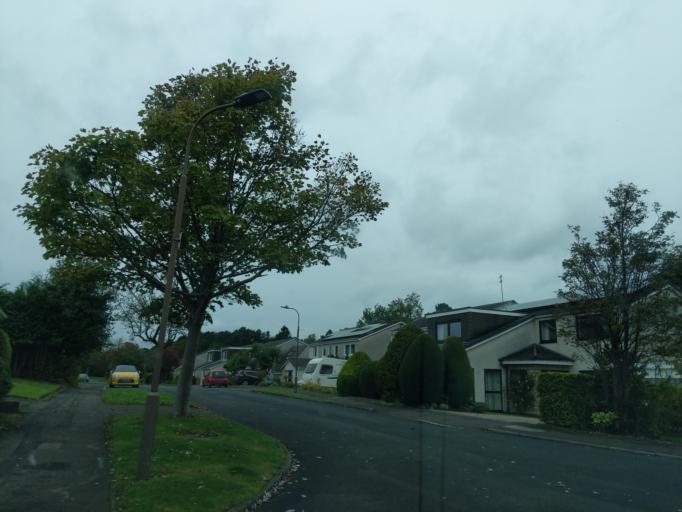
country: GB
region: Scotland
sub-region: Edinburgh
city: Balerno
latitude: 55.8796
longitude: -3.3468
